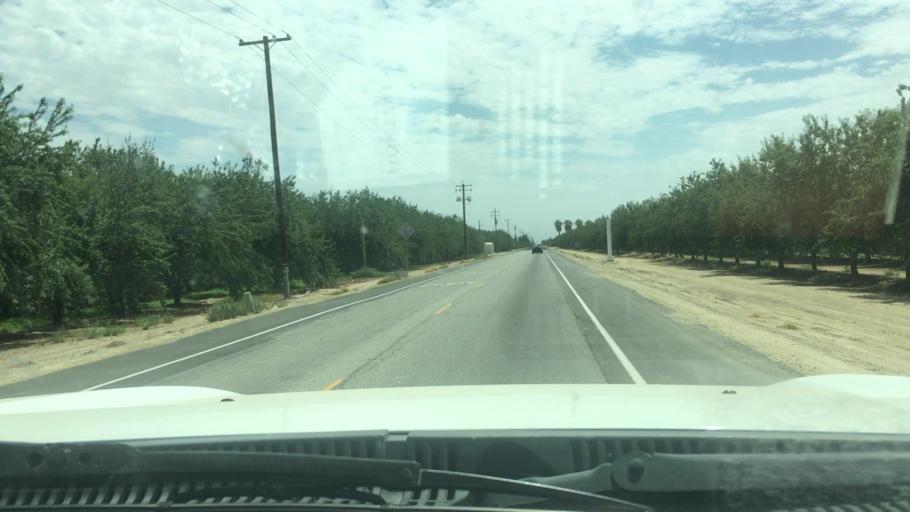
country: US
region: California
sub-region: Kern County
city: Wasco
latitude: 35.5580
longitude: -119.3477
